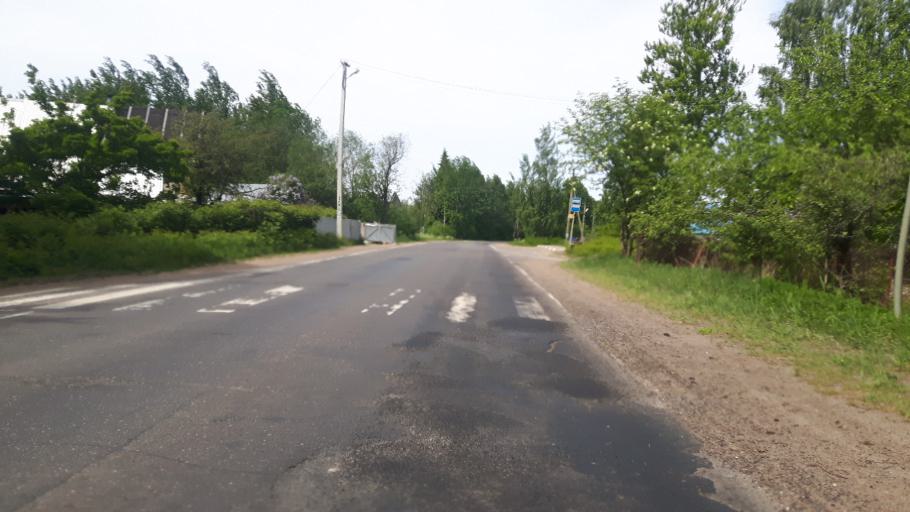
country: RU
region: Leningrad
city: Ust'-Luga
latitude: 59.6395
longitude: 28.2802
